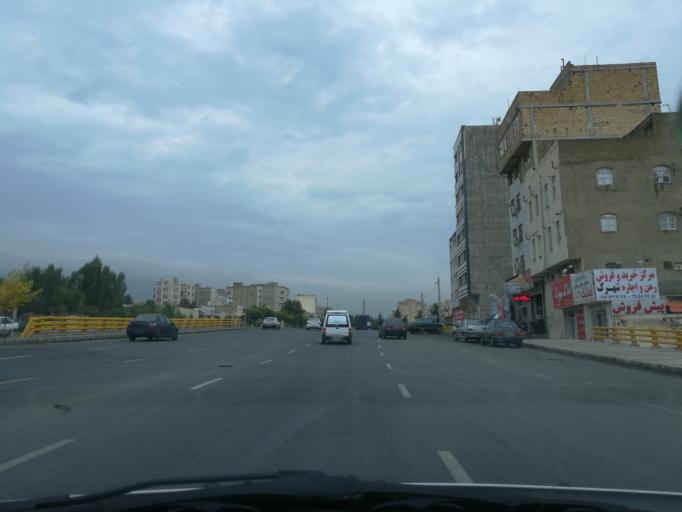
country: IR
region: Alborz
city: Karaj
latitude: 35.8617
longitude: 50.9369
